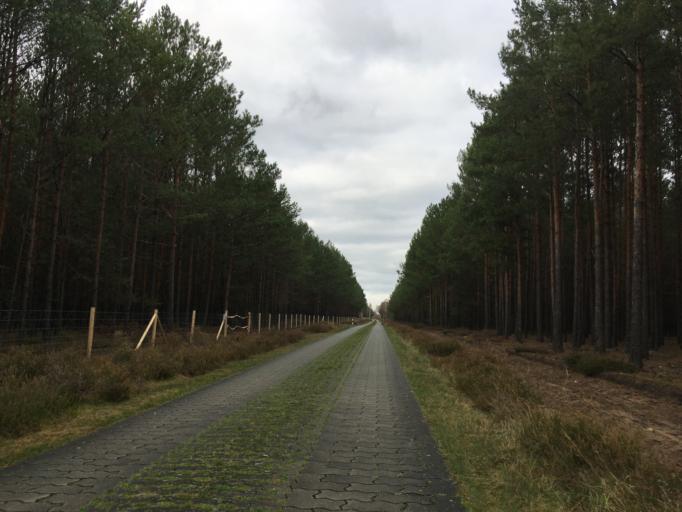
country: DE
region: Brandenburg
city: Tauer
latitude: 51.9966
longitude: 14.5121
